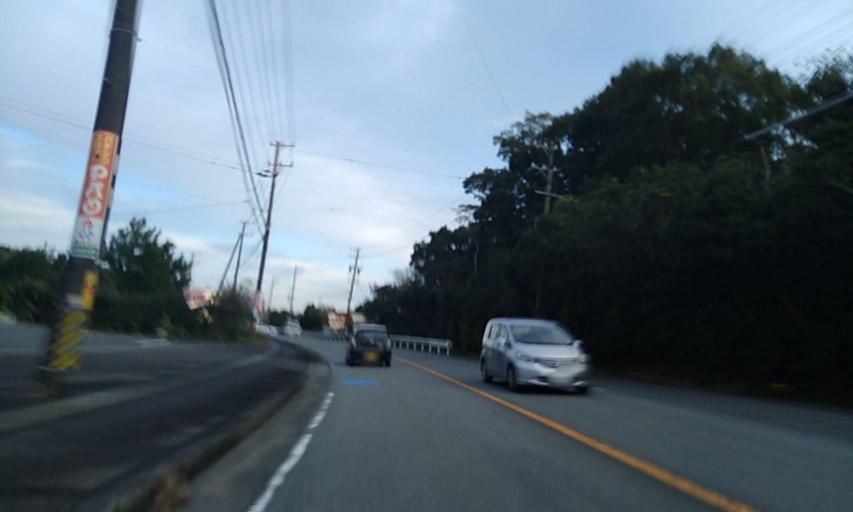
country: JP
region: Mie
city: Toba
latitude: 34.3136
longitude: 136.8605
